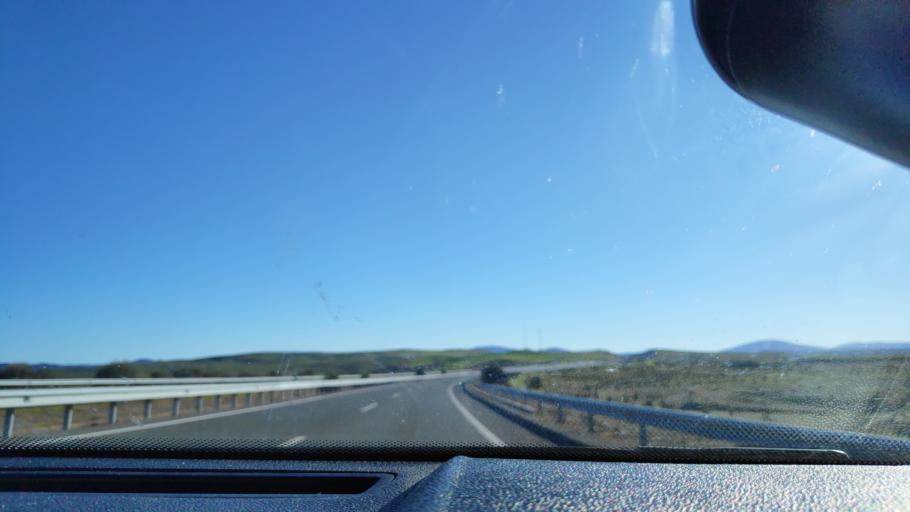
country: ES
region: Extremadura
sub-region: Provincia de Badajoz
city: Fuente de Cantos
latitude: 38.1733
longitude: -6.2787
